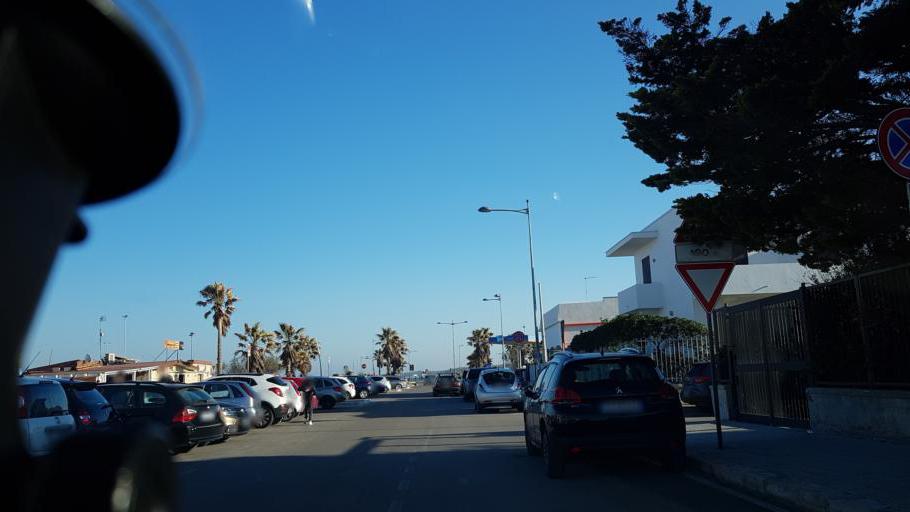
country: IT
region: Apulia
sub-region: Provincia di Lecce
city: Struda
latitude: 40.3911
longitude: 18.3052
